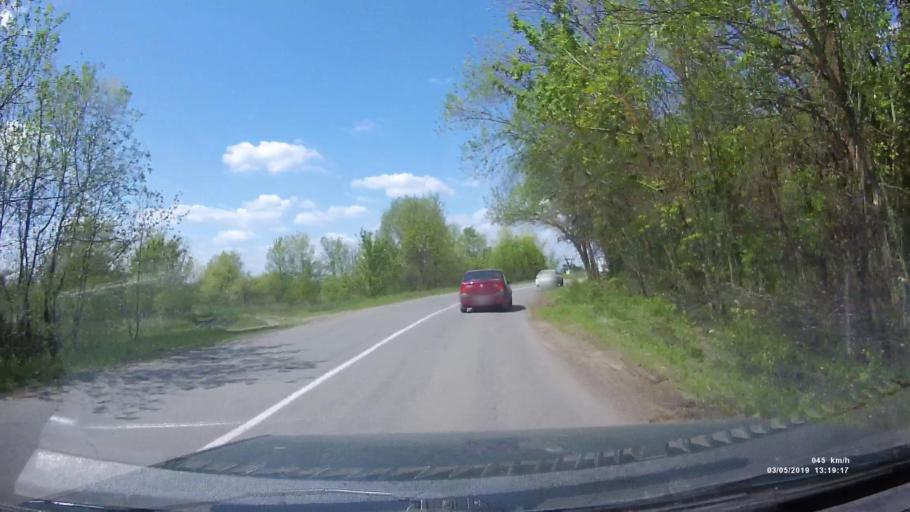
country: RU
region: Rostov
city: Semikarakorsk
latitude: 47.5365
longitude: 40.7478
